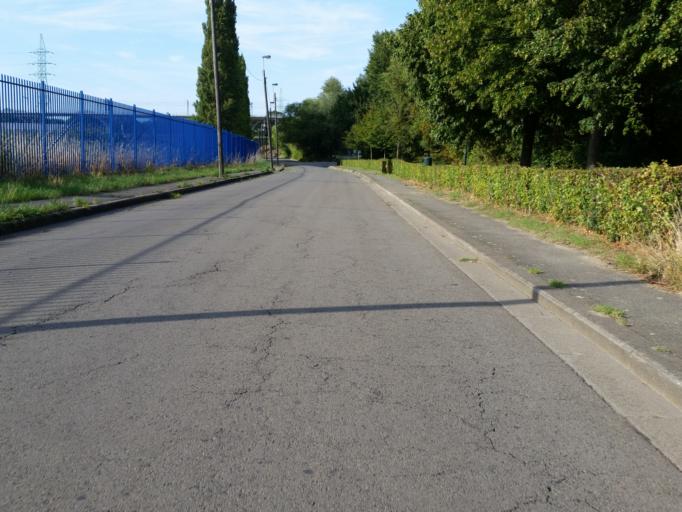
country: BE
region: Flanders
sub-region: Provincie Vlaams-Brabant
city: Diegem
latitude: 50.8976
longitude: 4.4183
